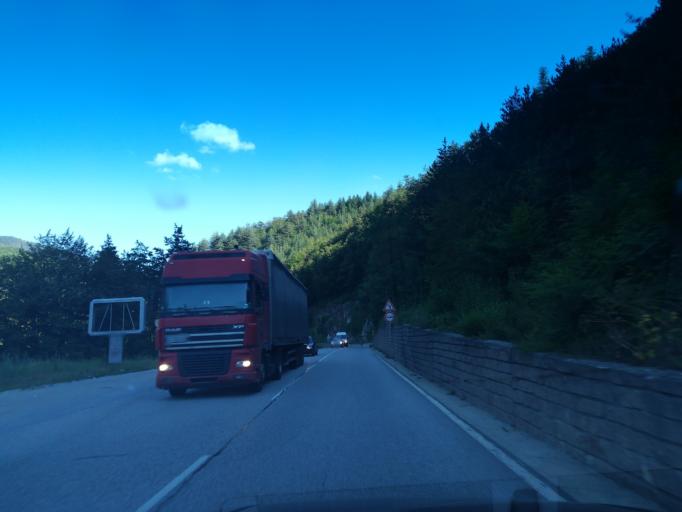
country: BG
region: Smolyan
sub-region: Obshtina Chepelare
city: Chepelare
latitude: 41.8280
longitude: 24.6867
